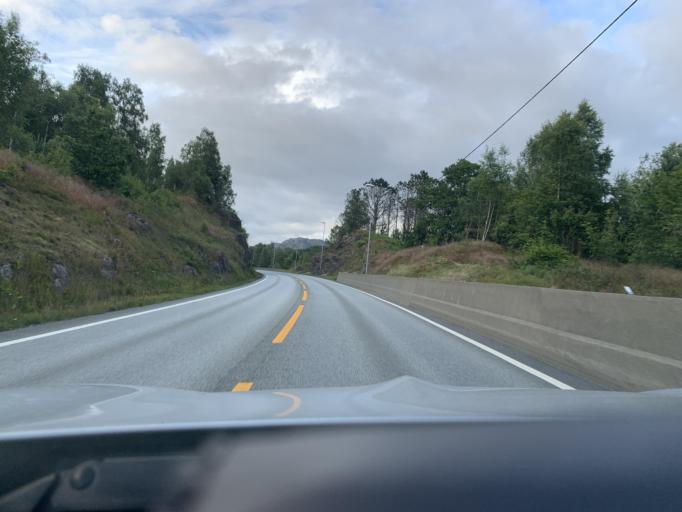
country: NO
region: Rogaland
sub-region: Bjerkreim
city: Vikesa
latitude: 58.5868
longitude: 6.0756
